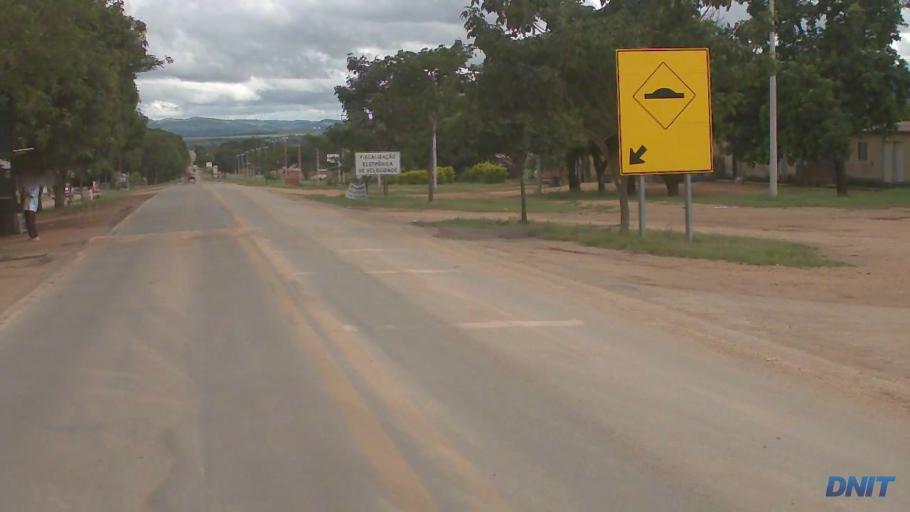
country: BR
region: Goias
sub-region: Padre Bernardo
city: Padre Bernardo
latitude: -15.2533
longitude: -48.2677
